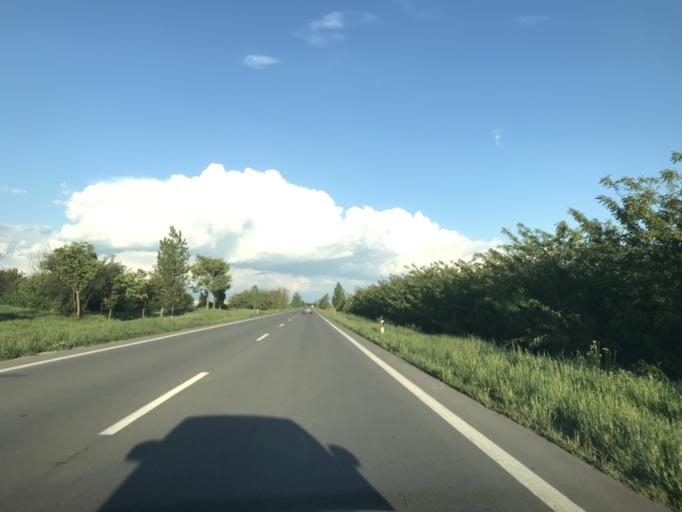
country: RS
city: Aradac
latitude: 45.3861
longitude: 20.3191
